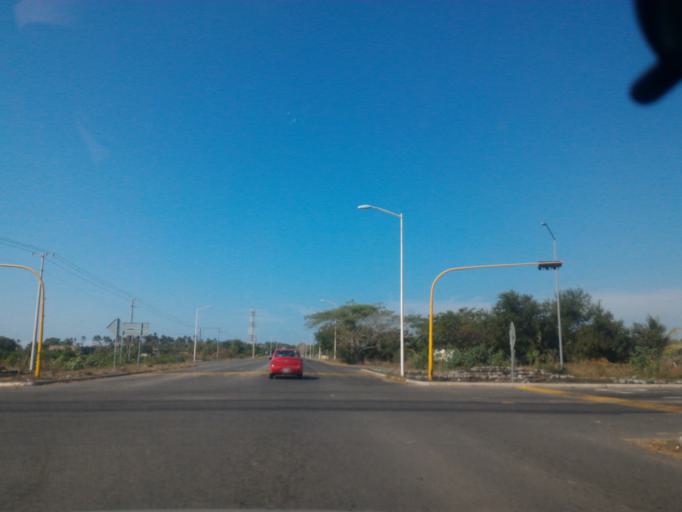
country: MX
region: Colima
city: Tecoman
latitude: 18.9034
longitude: -103.9058
